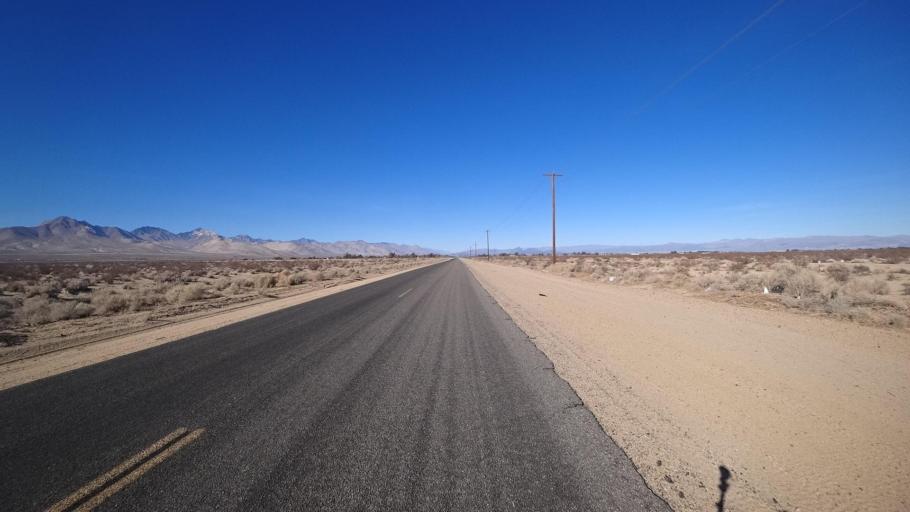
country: US
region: California
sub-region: Kern County
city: Inyokern
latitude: 35.6131
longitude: -117.8023
